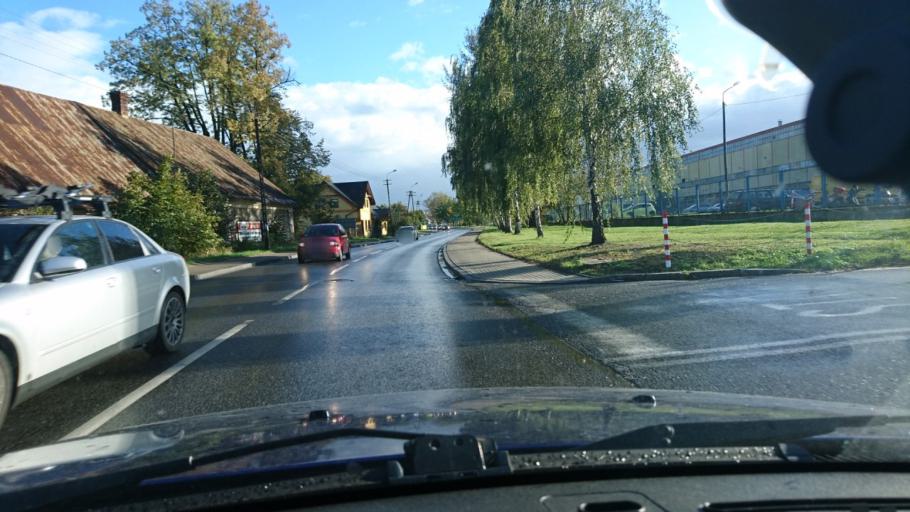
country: PL
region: Silesian Voivodeship
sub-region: Bielsko-Biala
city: Bielsko-Biala
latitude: 49.8439
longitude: 19.0502
